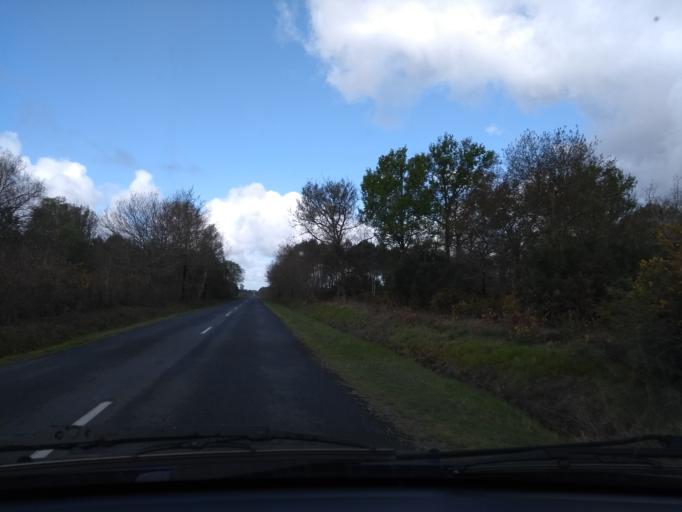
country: FR
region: Aquitaine
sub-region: Departement de la Gironde
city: Mios
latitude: 44.5507
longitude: -0.9555
